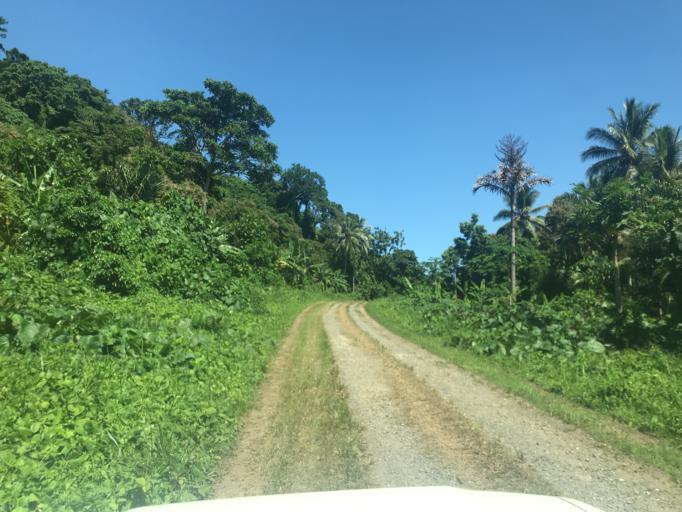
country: VU
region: Sanma
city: Luganville
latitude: -15.6011
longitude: 166.7829
